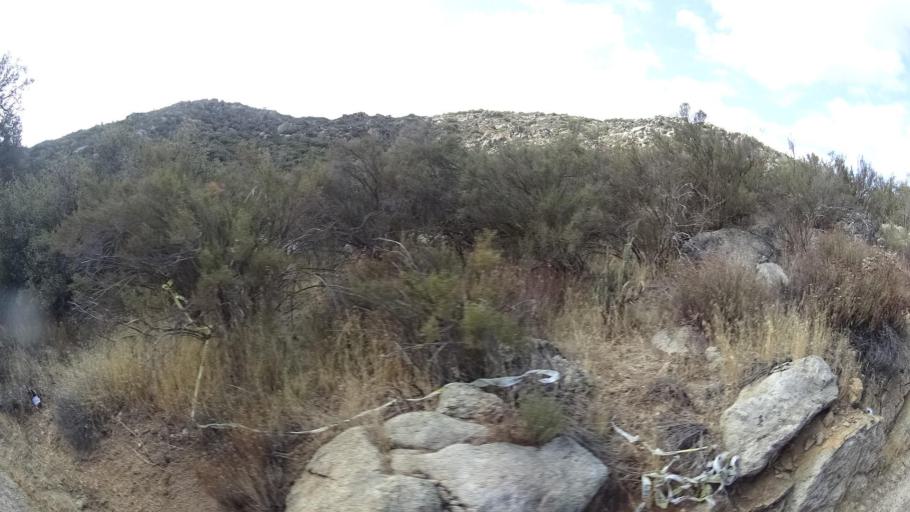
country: US
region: California
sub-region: San Diego County
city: Campo
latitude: 32.7062
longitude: -116.4906
